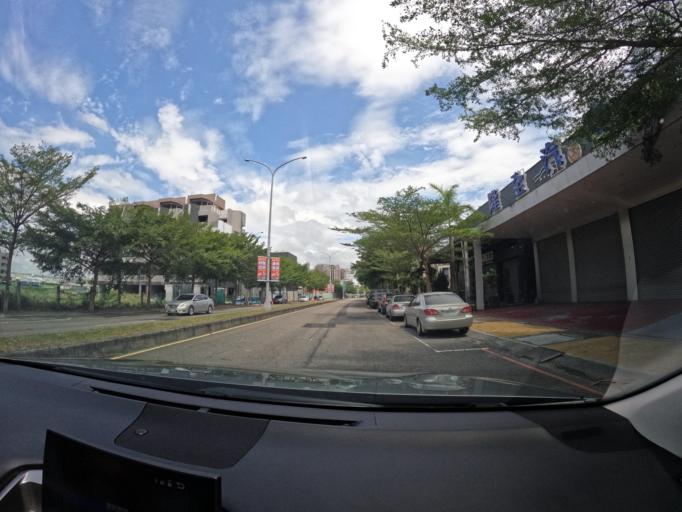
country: TW
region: Taiwan
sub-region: Taichung City
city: Taichung
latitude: 24.1370
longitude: 120.6263
